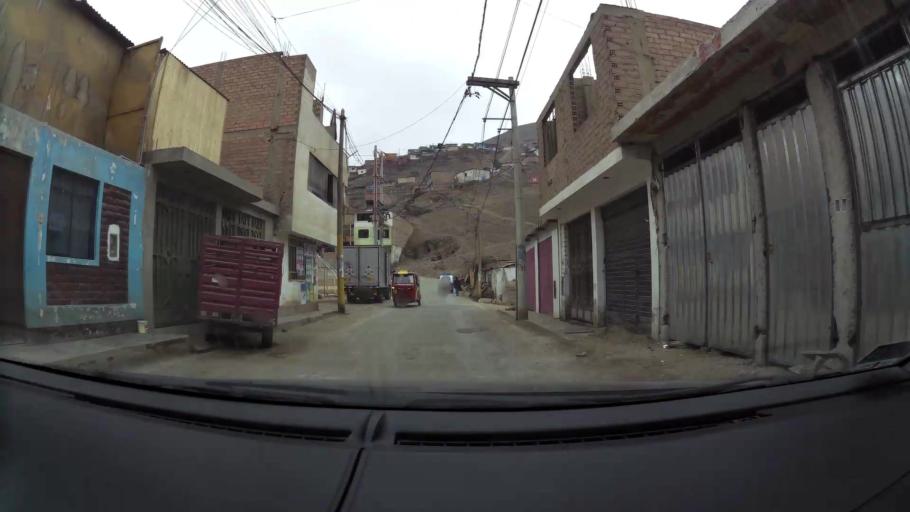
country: PE
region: Lima
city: Ventanilla
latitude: -11.9178
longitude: -77.0919
